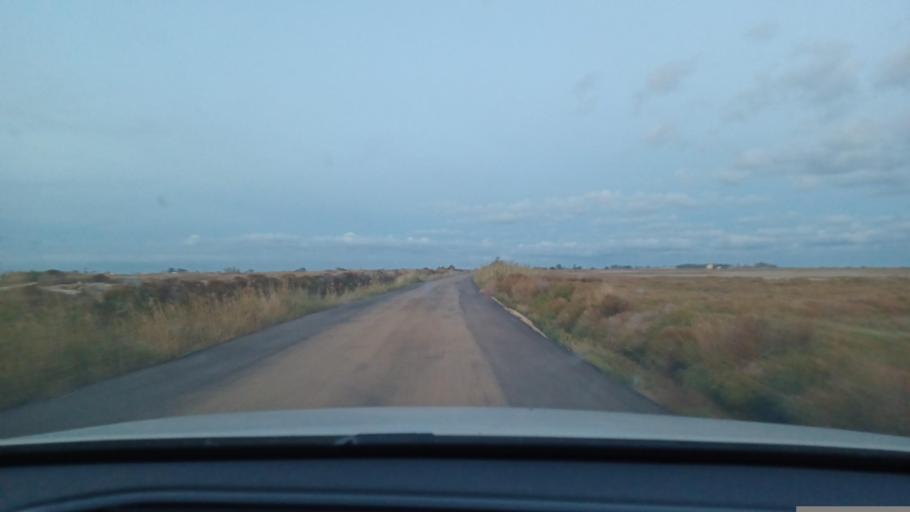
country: ES
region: Catalonia
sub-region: Provincia de Tarragona
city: Deltebre
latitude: 40.6432
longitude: 0.7537
